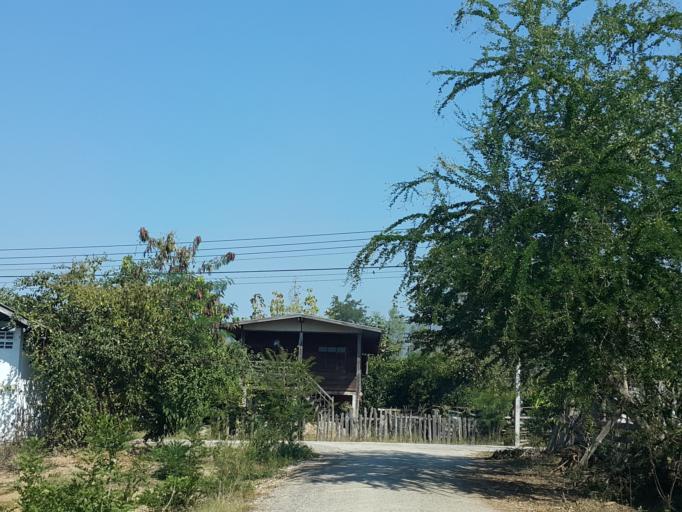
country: TH
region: Sukhothai
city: Thung Saliam
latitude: 17.3447
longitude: 99.4419
